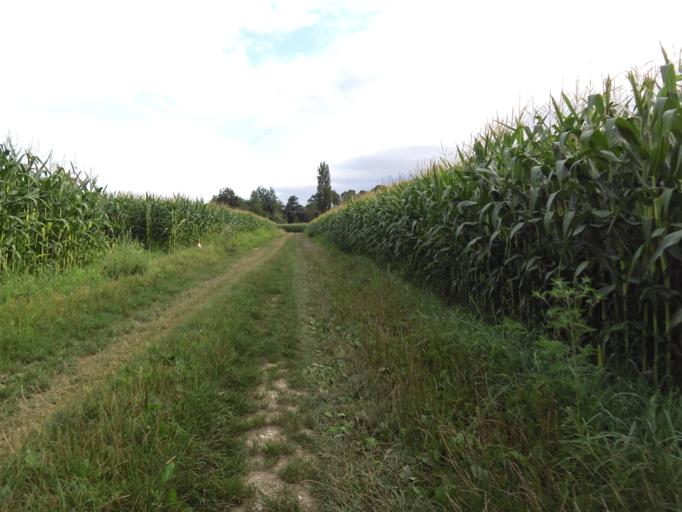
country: FR
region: Rhone-Alpes
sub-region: Departement de l'Ain
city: Chazey-sur-Ain
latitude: 45.9282
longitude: 5.2364
